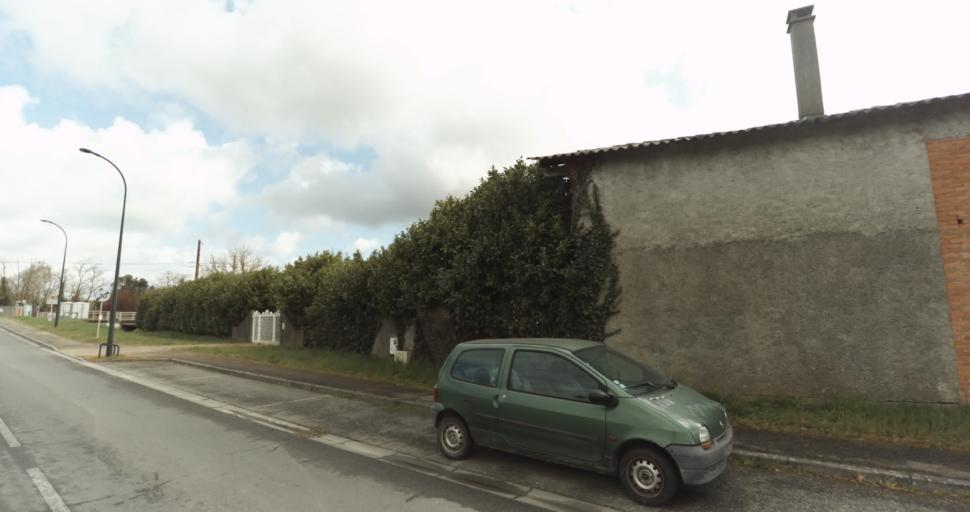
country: FR
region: Midi-Pyrenees
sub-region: Departement de la Haute-Garonne
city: Auterive
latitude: 43.3454
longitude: 1.4705
